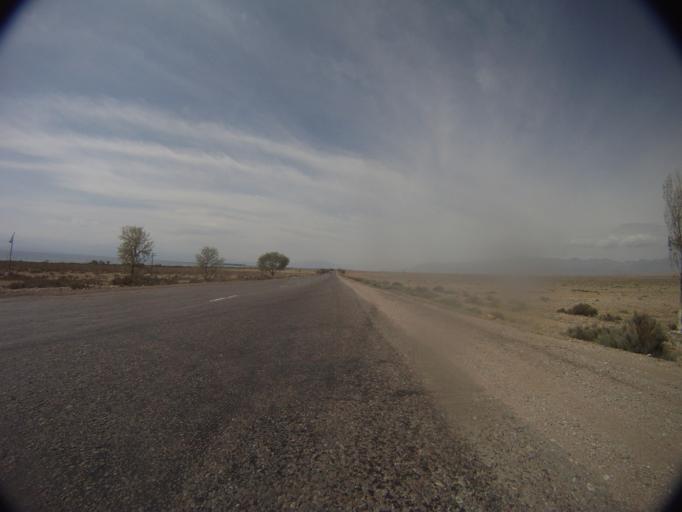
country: KG
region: Ysyk-Koel
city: Balykchy
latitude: 42.5147
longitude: 76.5309
